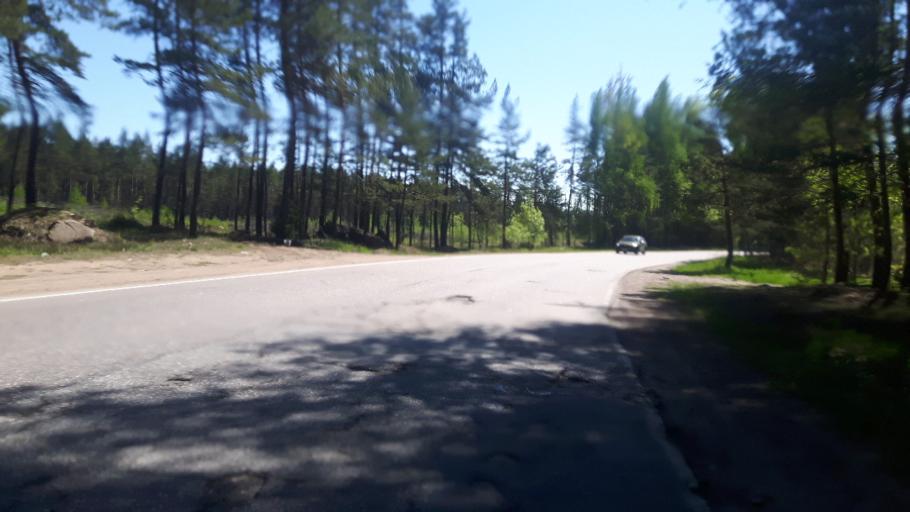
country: RU
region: Leningrad
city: Glebychevo
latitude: 60.3453
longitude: 28.8221
